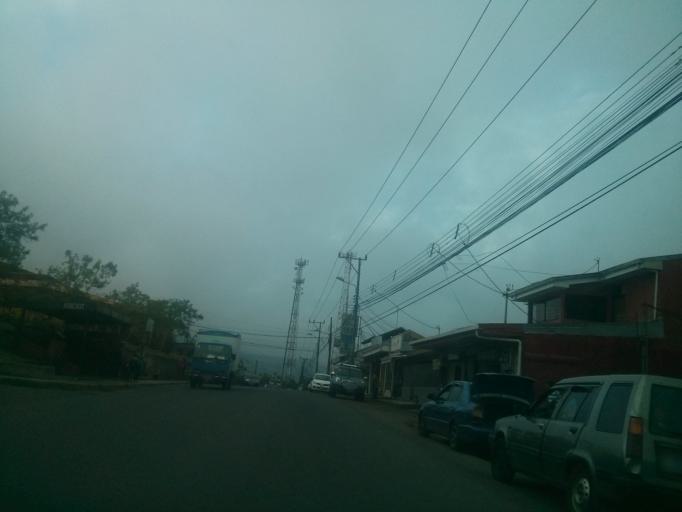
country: CR
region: Cartago
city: Cot
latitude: 9.8858
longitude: -83.8079
